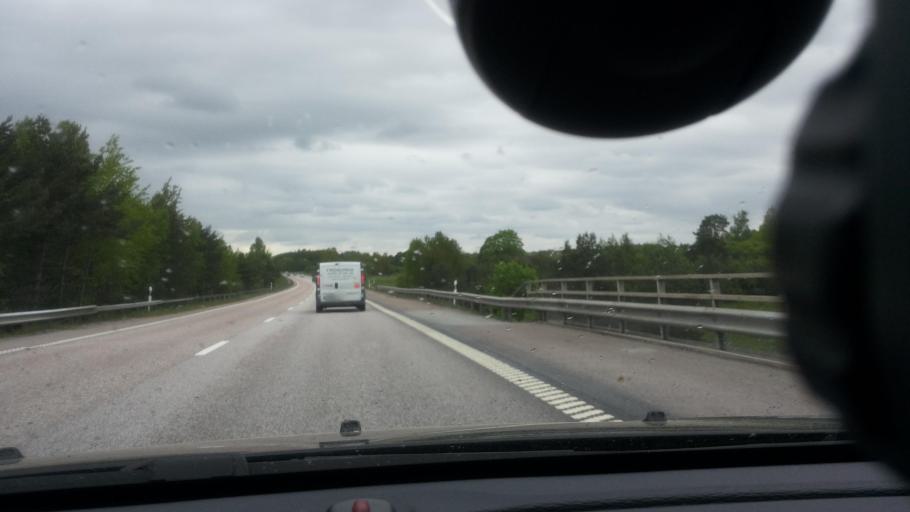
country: SE
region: Stockholm
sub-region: Sigtuna Kommun
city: Marsta
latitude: 59.6306
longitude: 17.9002
